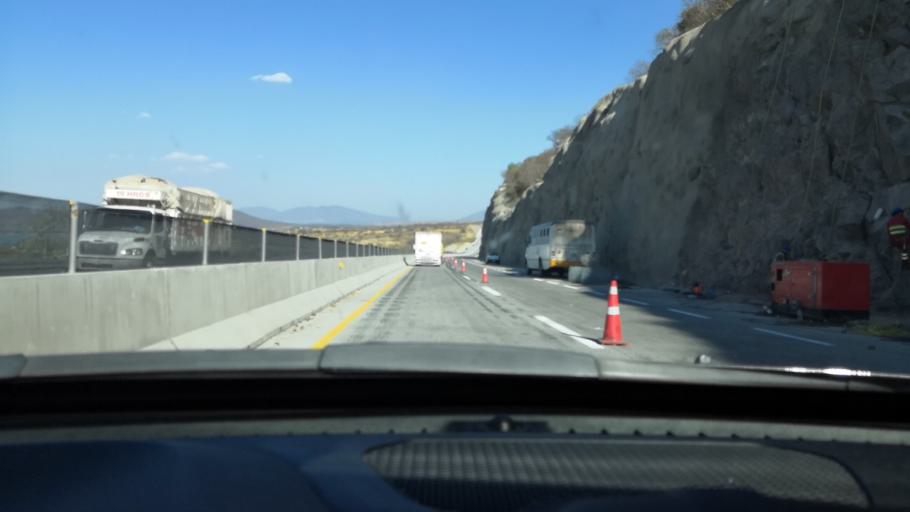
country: MX
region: Jalisco
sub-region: Tlajomulco de Zuniga
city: San Lucas Evangelista
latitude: 20.3916
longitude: -103.3335
